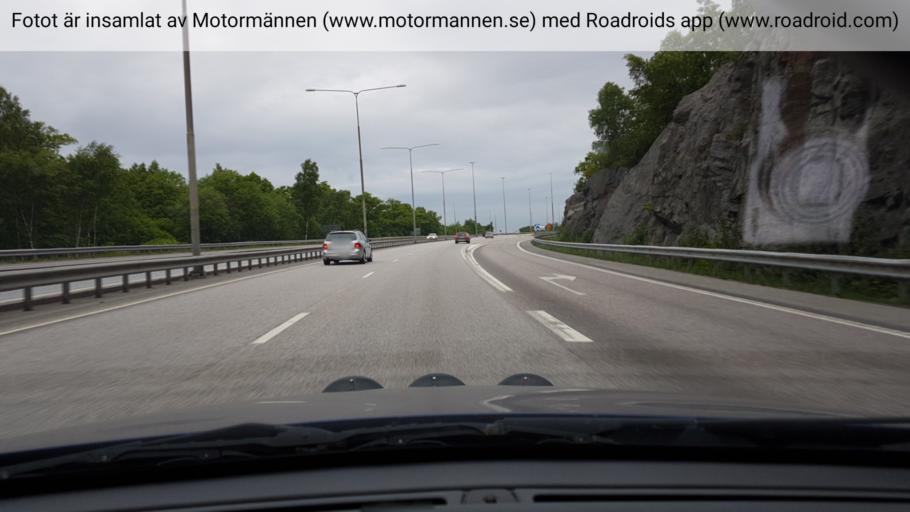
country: SE
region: Stockholm
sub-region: Haninge Kommun
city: Handen
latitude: 59.2255
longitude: 18.1281
